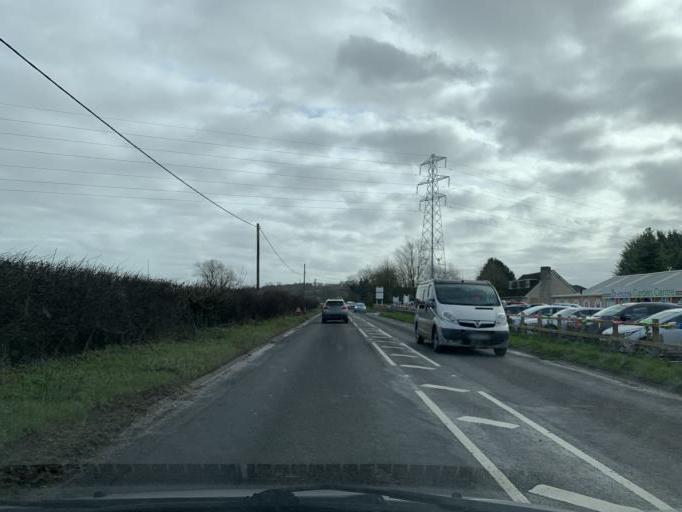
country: GB
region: England
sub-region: Wiltshire
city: Wilton
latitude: 51.0638
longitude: -1.8376
